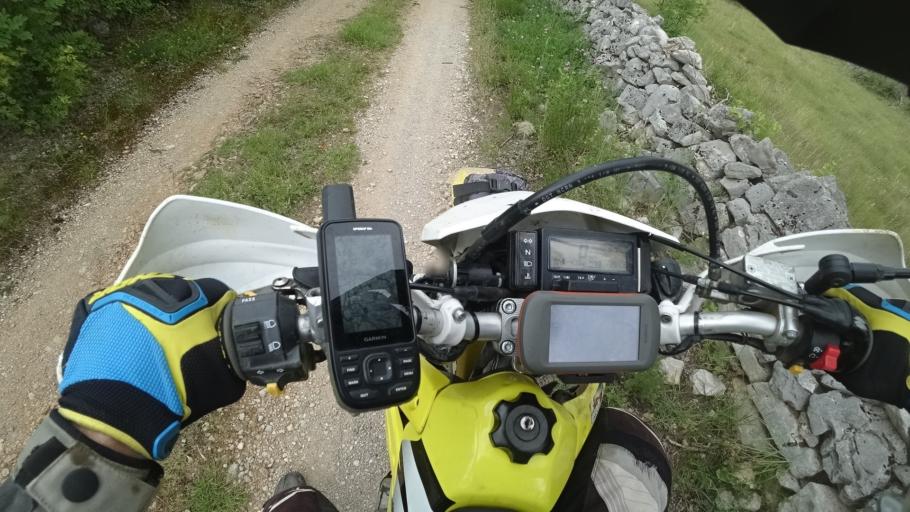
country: HR
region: Sibensko-Kniniska
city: Knin
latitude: 44.0158
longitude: 16.2702
